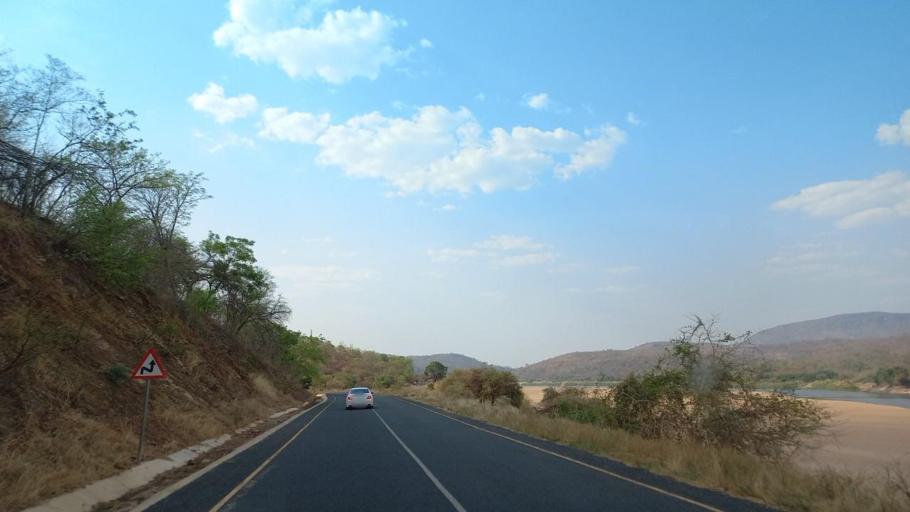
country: ZM
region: Lusaka
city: Luangwa
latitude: -15.0012
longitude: 30.2153
